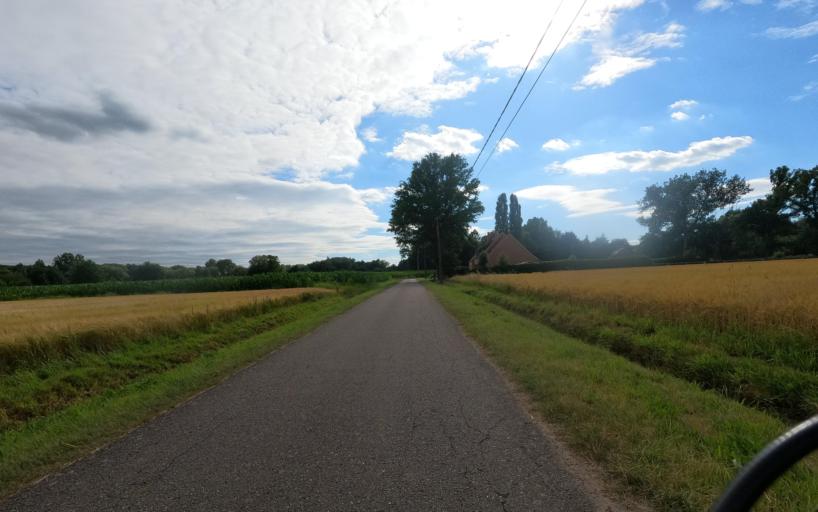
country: BE
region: Flanders
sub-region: Provincie Vlaams-Brabant
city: Tremelo
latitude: 51.0220
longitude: 4.7366
